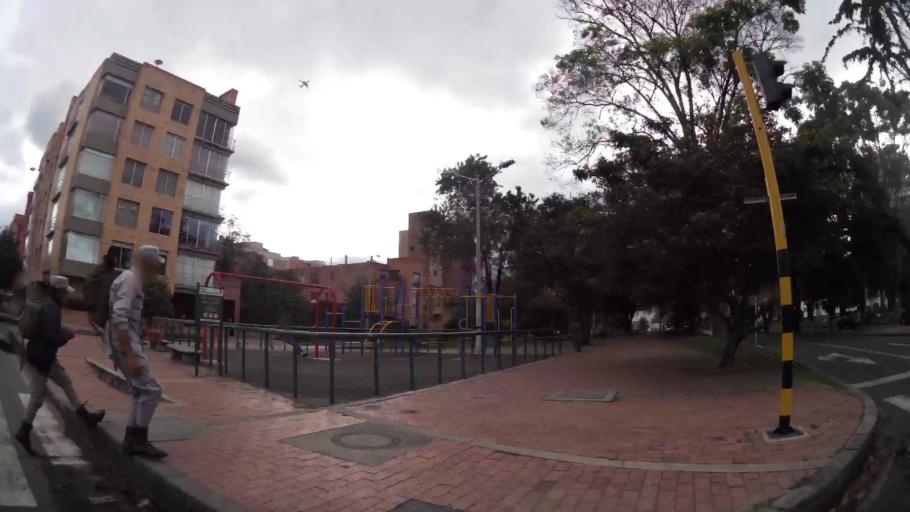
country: CO
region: Bogota D.C.
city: Barrio San Luis
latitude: 4.6892
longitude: -74.0436
